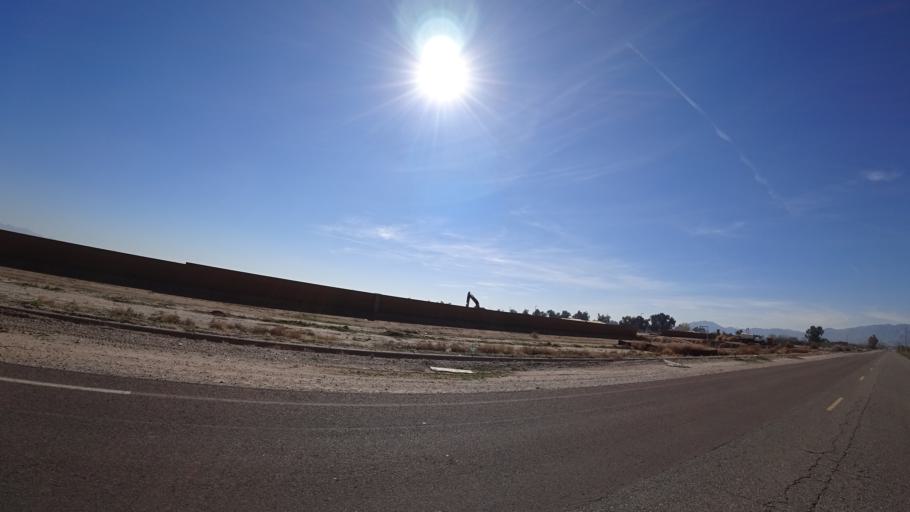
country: US
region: Arizona
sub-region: Maricopa County
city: Citrus Park
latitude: 33.5082
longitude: -112.4570
